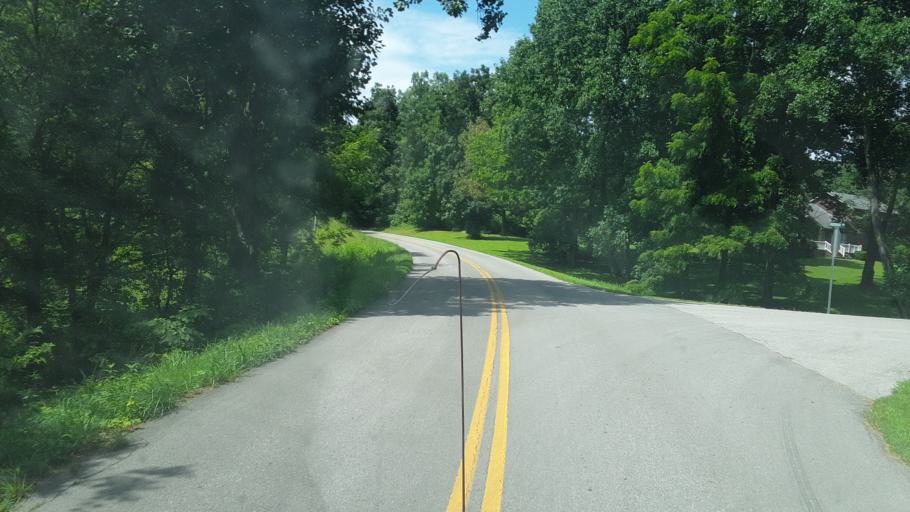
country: US
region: Kentucky
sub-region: Christian County
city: Oak Grove
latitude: 36.7315
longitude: -87.3355
